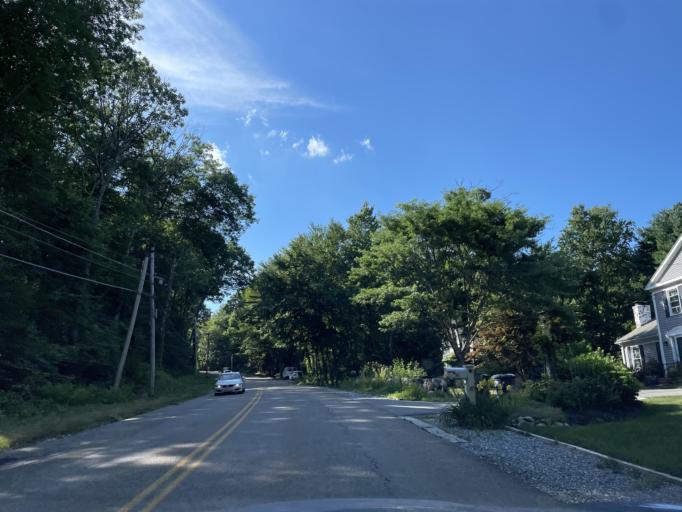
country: US
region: Massachusetts
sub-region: Worcester County
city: Oxford
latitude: 42.1217
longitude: -71.9181
